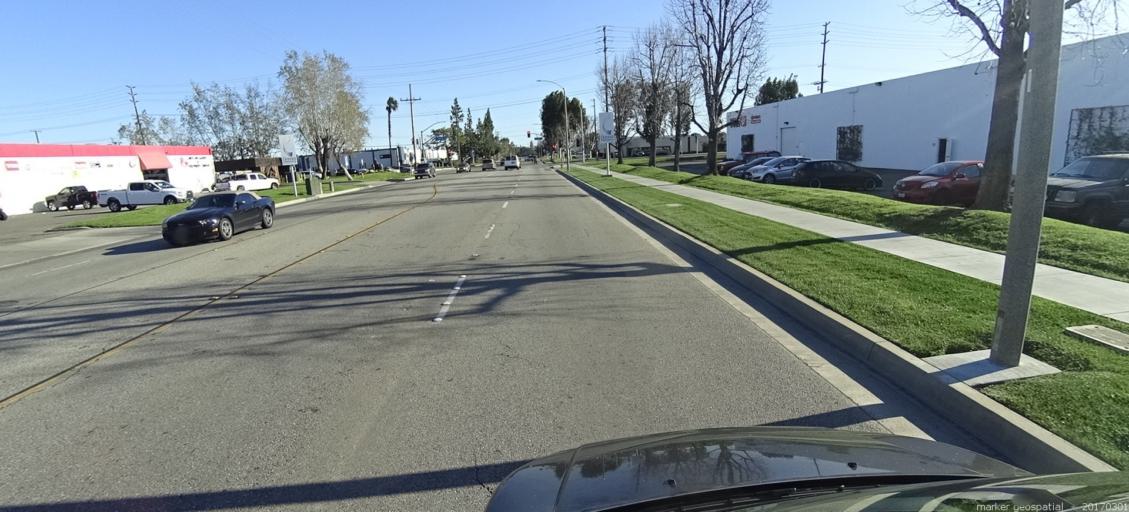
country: US
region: California
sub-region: Orange County
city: Placentia
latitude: 33.8559
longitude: -117.8727
